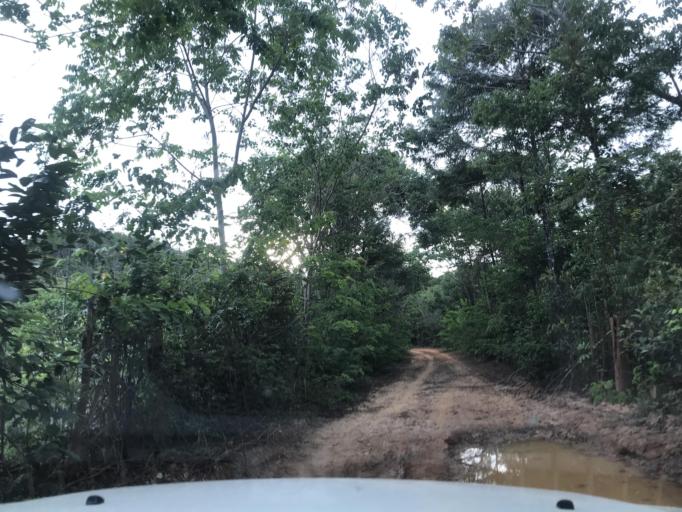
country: BR
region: Bahia
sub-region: Entre Rios
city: Entre Rios
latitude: -12.0520
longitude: -38.2174
